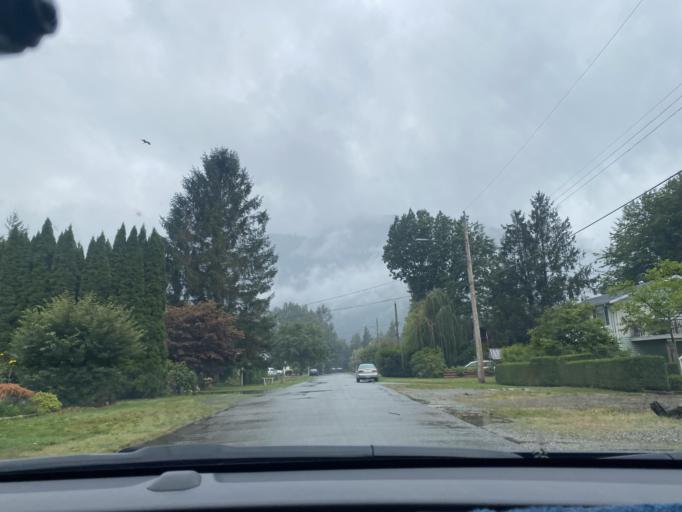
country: CA
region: British Columbia
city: Agassiz
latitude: 49.3020
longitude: -121.7744
